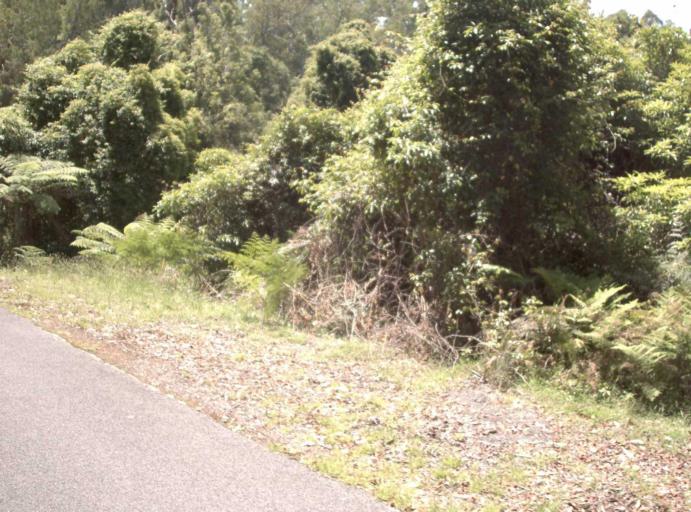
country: AU
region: New South Wales
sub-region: Bombala
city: Bombala
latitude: -37.4909
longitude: 148.9253
